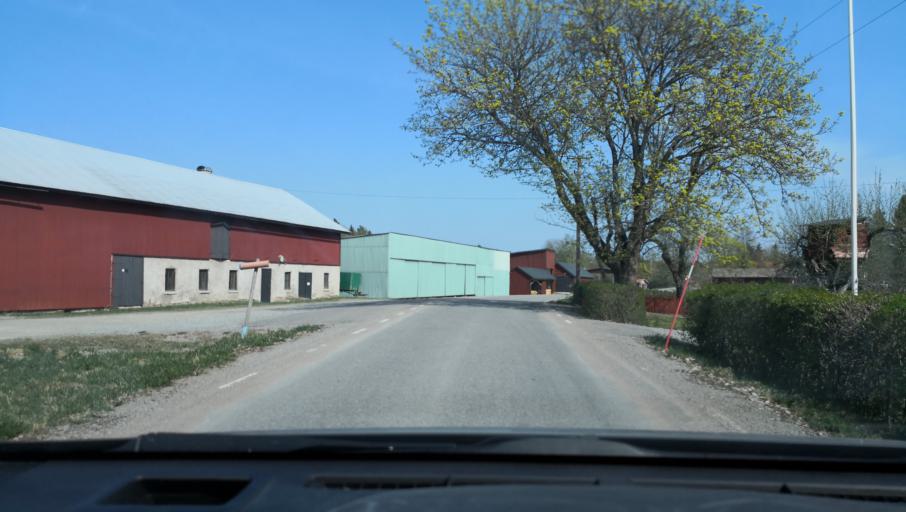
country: SE
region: Vaestmanland
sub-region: Sala Kommun
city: Sala
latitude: 60.0068
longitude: 16.6977
